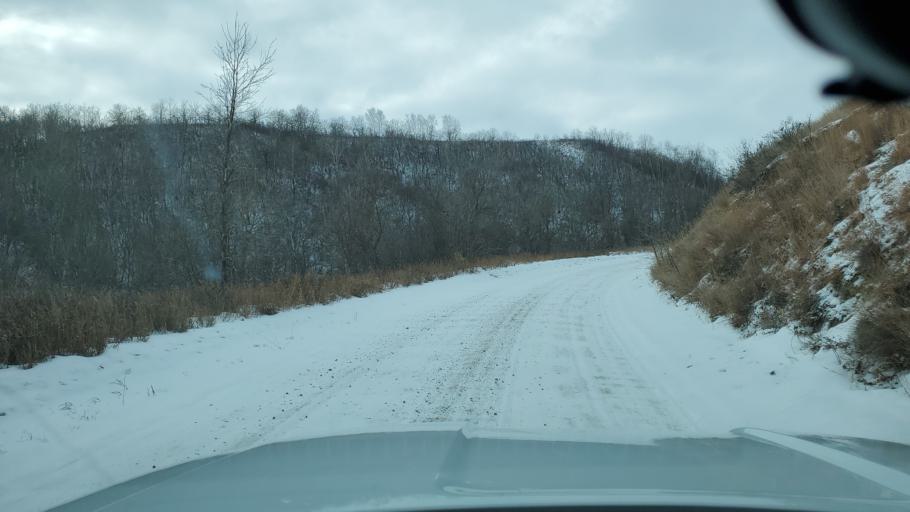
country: CA
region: Saskatchewan
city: White City
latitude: 50.7720
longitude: -104.1437
